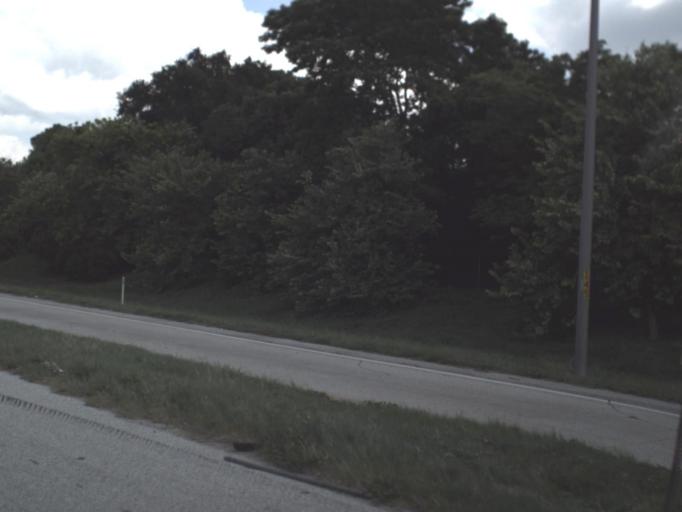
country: US
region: Florida
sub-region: Pinellas County
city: Saint Petersburg
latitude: 27.7949
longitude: -82.6609
